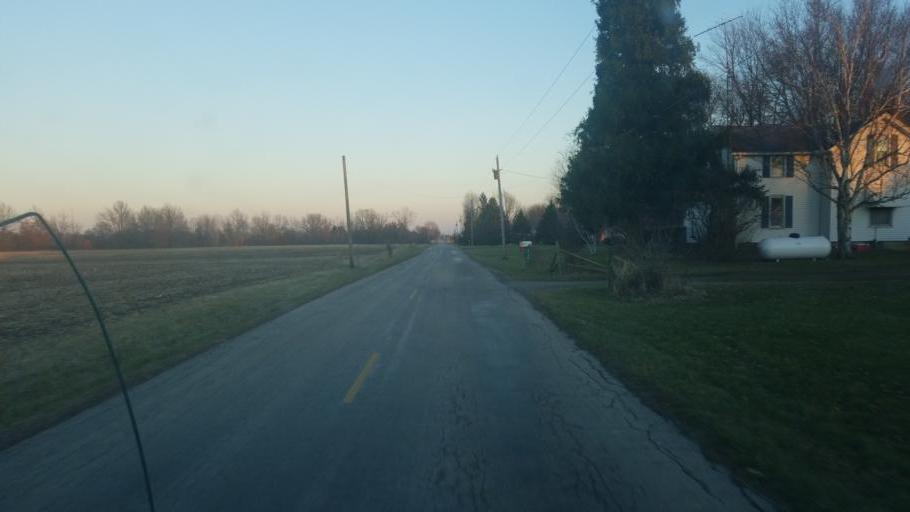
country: US
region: Ohio
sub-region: Marion County
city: Marion
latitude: 40.6222
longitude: -83.2849
